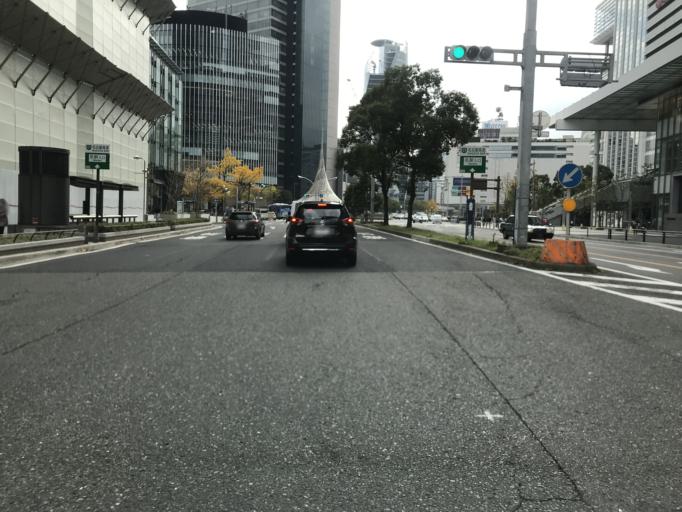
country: JP
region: Aichi
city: Nagoya-shi
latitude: 35.1724
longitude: 136.8831
